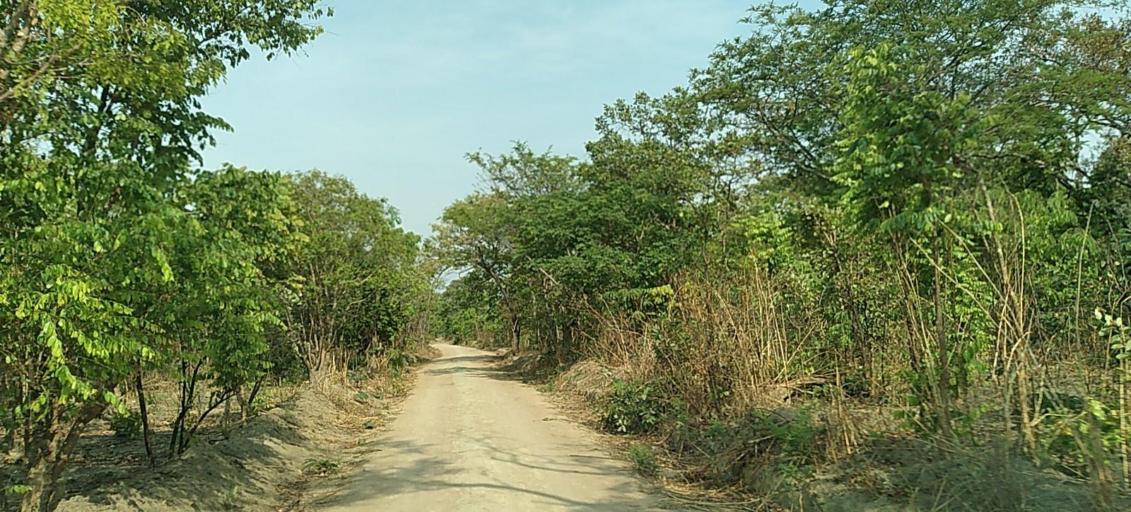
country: ZM
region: Copperbelt
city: Luanshya
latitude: -13.2211
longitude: 28.6663
